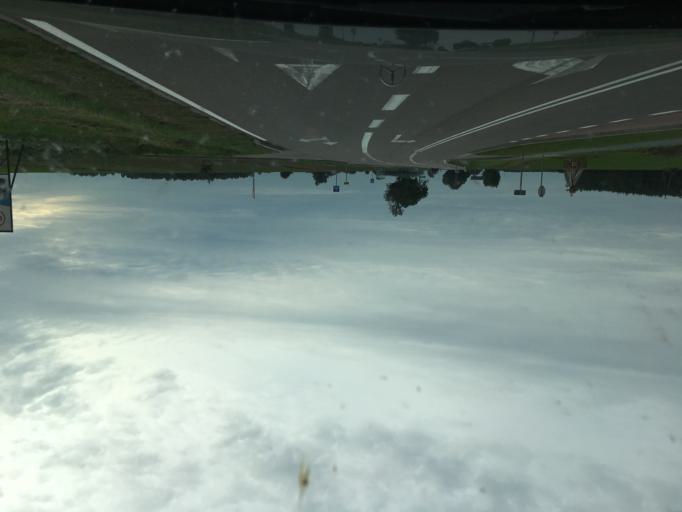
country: PL
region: Masovian Voivodeship
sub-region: Powiat ostrowski
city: Ostrow Mazowiecka
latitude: 52.8852
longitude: 21.8647
